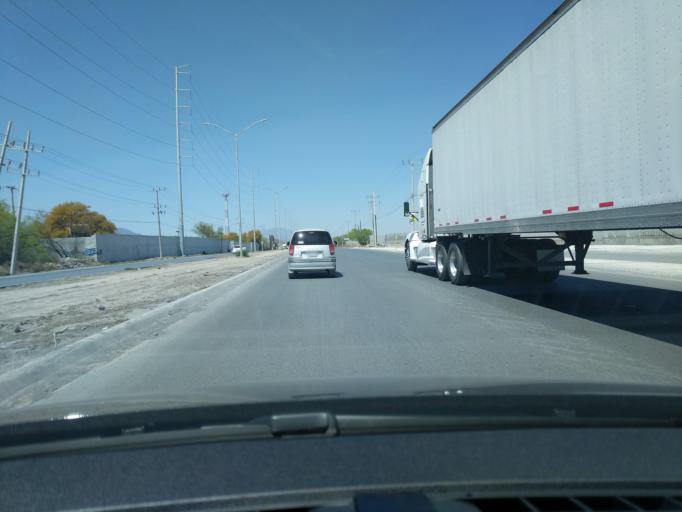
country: MX
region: Nuevo Leon
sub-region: Salinas Victoria
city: Emiliano Zapata
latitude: 25.9004
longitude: -100.2626
